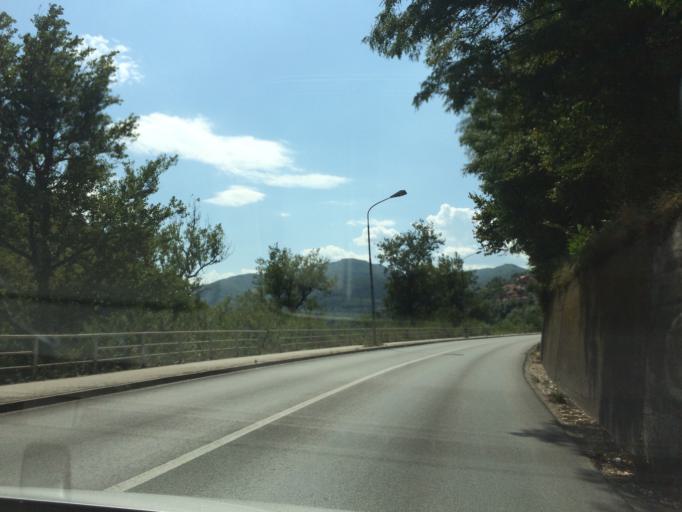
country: RS
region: Central Serbia
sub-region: Zlatiborski Okrug
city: Prijepolje
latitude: 43.3798
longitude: 19.6349
